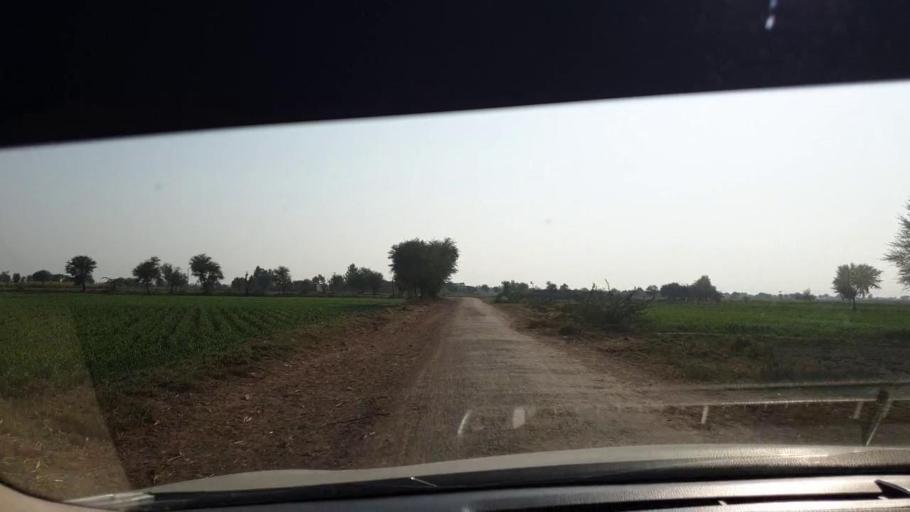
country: PK
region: Sindh
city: Berani
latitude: 25.8147
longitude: 68.7766
